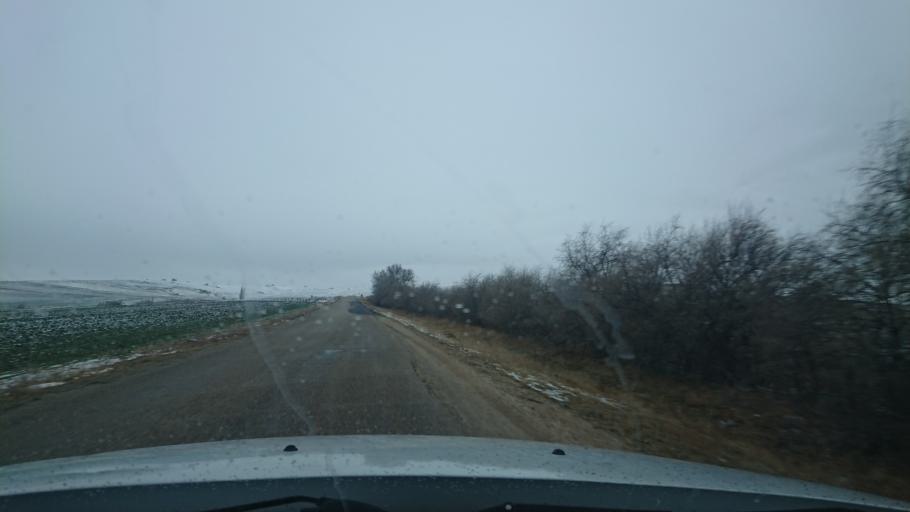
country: TR
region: Aksaray
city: Agacoren
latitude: 38.8510
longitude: 33.9505
